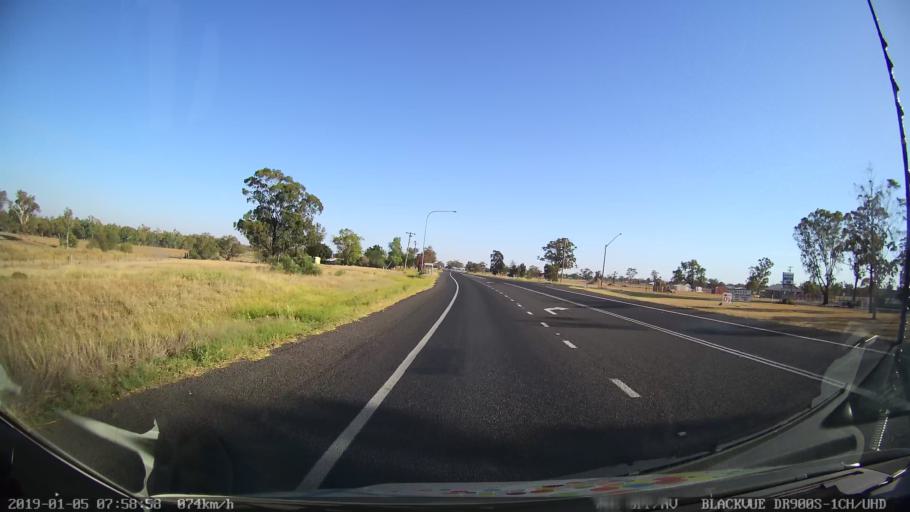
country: AU
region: New South Wales
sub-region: Gilgandra
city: Gilgandra
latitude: -31.7076
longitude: 148.6793
